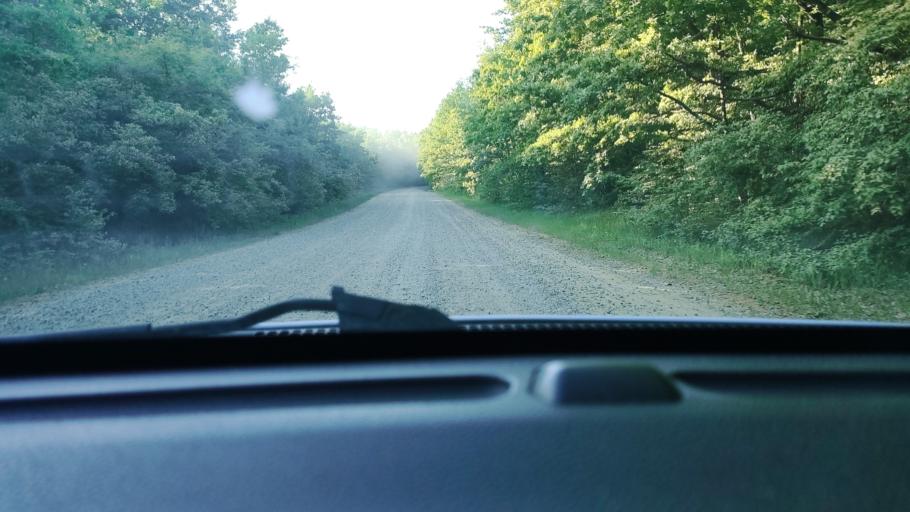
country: RU
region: Krasnodarskiy
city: Goryachiy Klyuch
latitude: 44.7114
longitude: 38.9919
